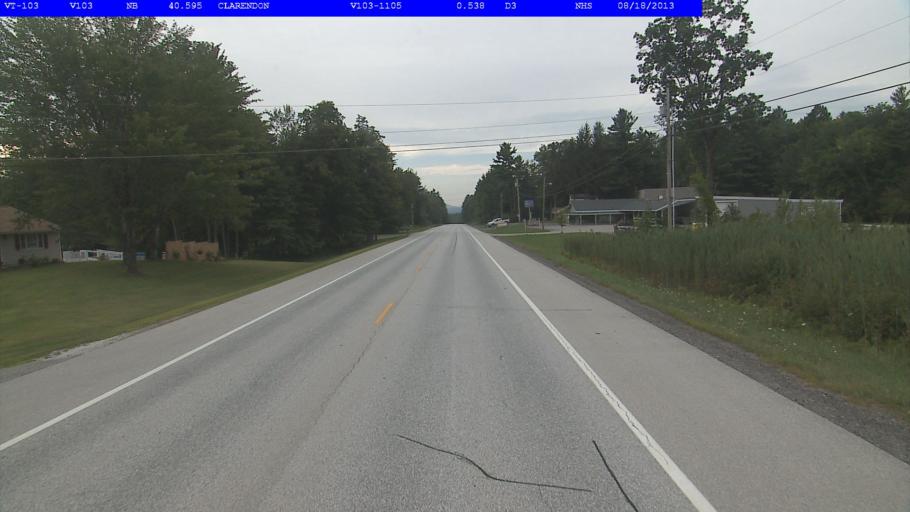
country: US
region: Vermont
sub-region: Rutland County
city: Rutland
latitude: 43.5303
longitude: -72.9368
